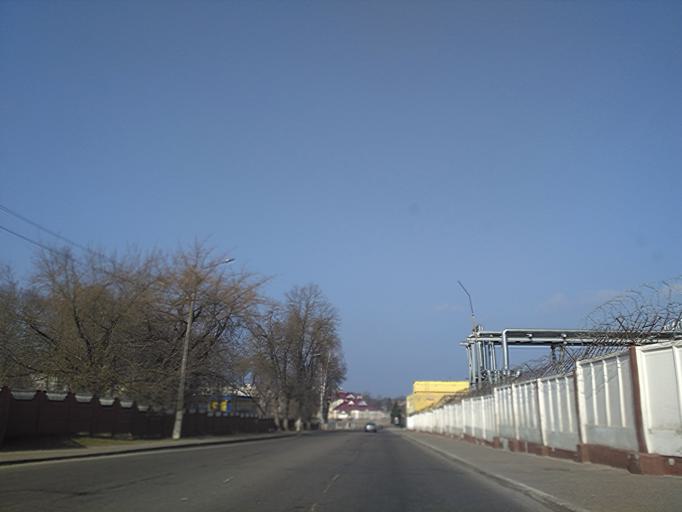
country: BY
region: Minsk
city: Horad Barysaw
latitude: 54.2262
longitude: 28.5257
